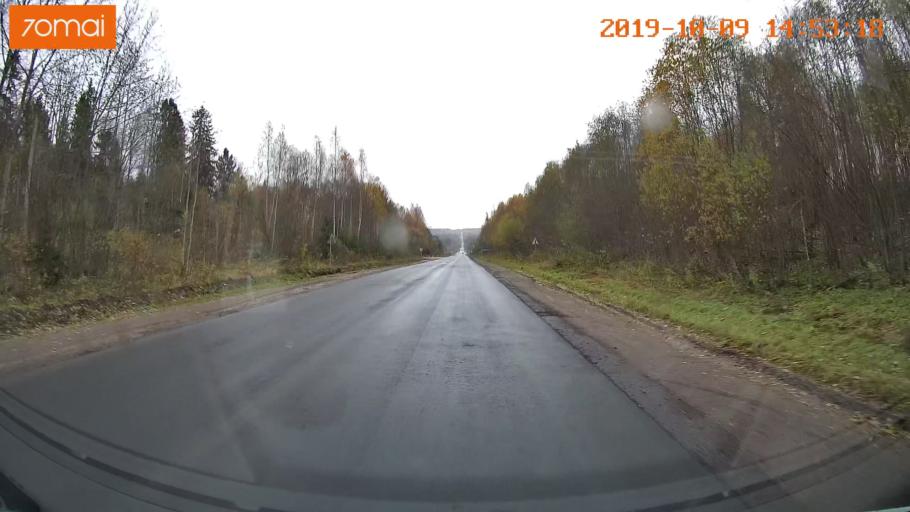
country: RU
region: Kostroma
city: Chistyye Bory
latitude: 58.3694
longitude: 41.6376
